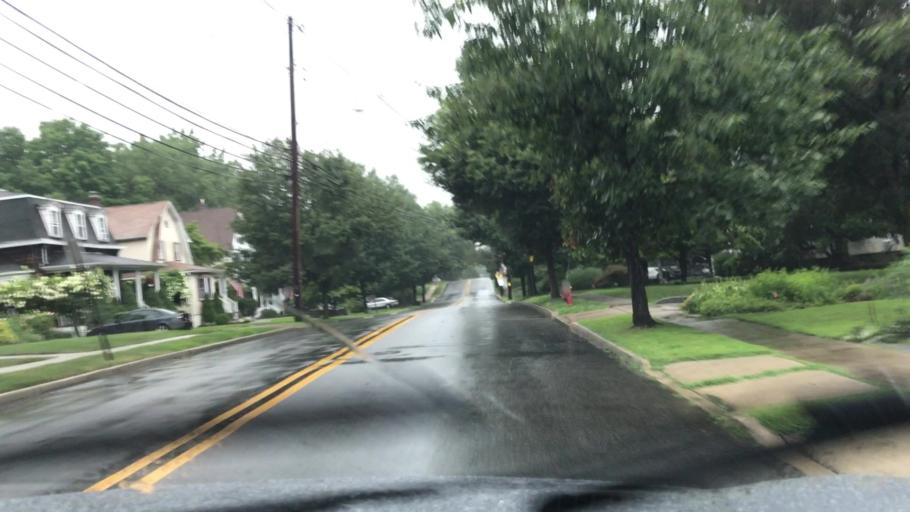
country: US
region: New Jersey
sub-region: Bergen County
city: Closter
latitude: 40.9725
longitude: -73.9639
